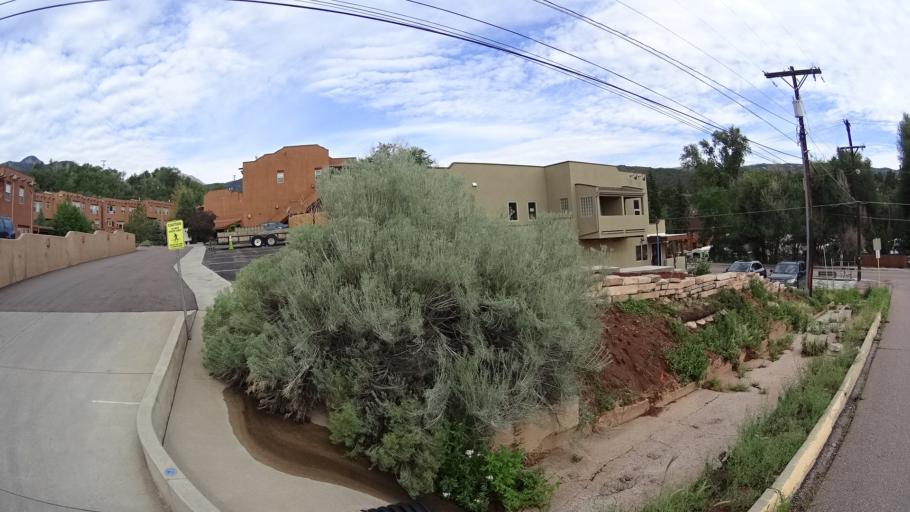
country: US
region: Colorado
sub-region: El Paso County
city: Manitou Springs
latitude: 38.8563
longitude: -104.9002
